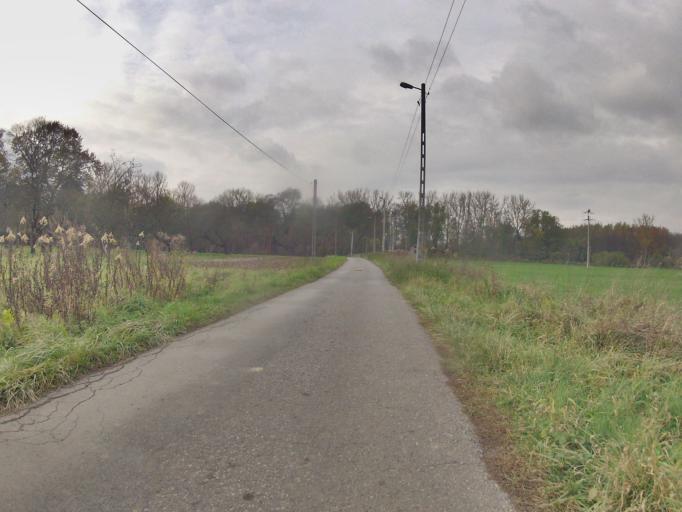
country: PL
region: Lesser Poland Voivodeship
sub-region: Powiat wielicki
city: Wegrzce Wielkie
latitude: 50.0462
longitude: 20.1024
